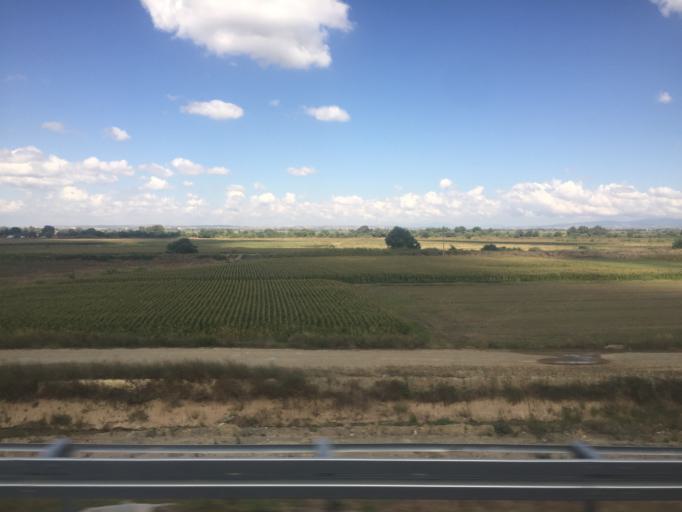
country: TR
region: Bursa
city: Karacabey
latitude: 40.1267
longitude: 28.2863
